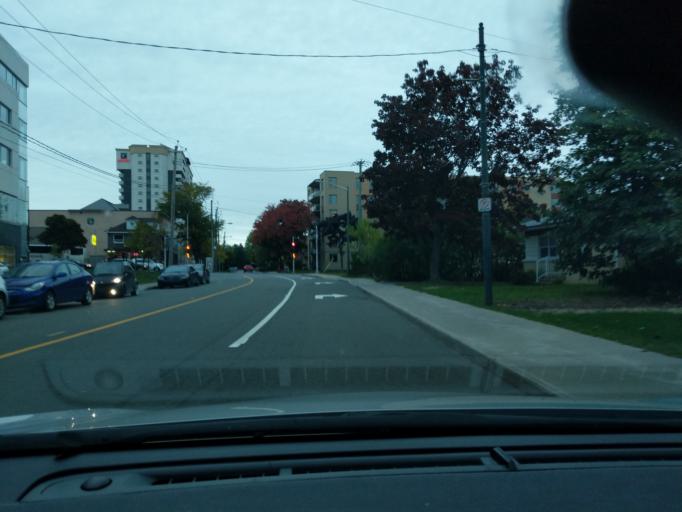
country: CA
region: Quebec
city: L'Ancienne-Lorette
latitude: 46.7658
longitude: -71.2886
